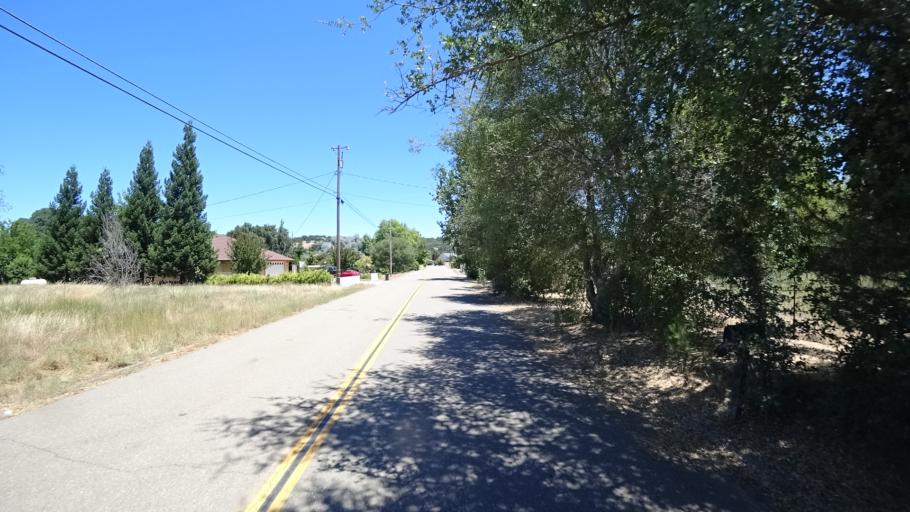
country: US
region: California
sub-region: Calaveras County
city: Rancho Calaveras
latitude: 38.1572
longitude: -120.8469
